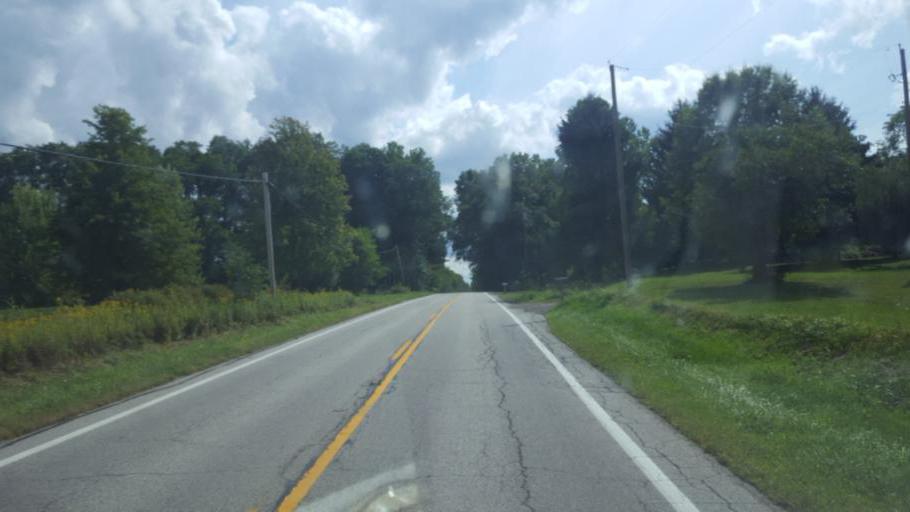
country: US
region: Ohio
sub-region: Portage County
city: Hiram
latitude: 41.3644
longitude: -81.1431
